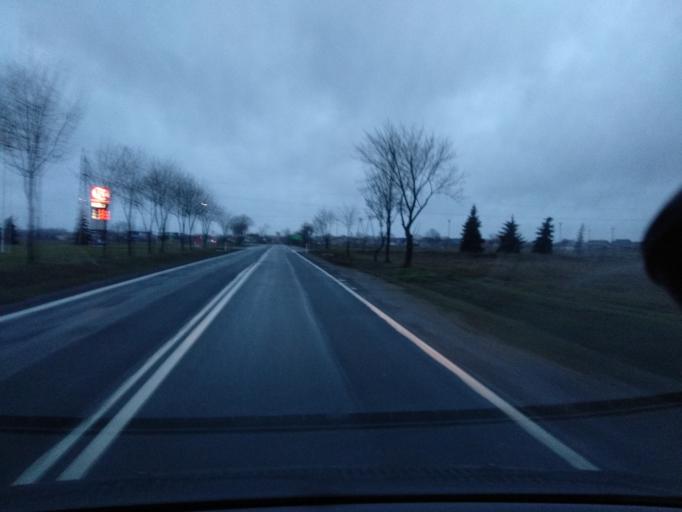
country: PL
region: Lower Silesian Voivodeship
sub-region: Powiat legnicki
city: Prochowice
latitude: 51.2674
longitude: 16.3776
